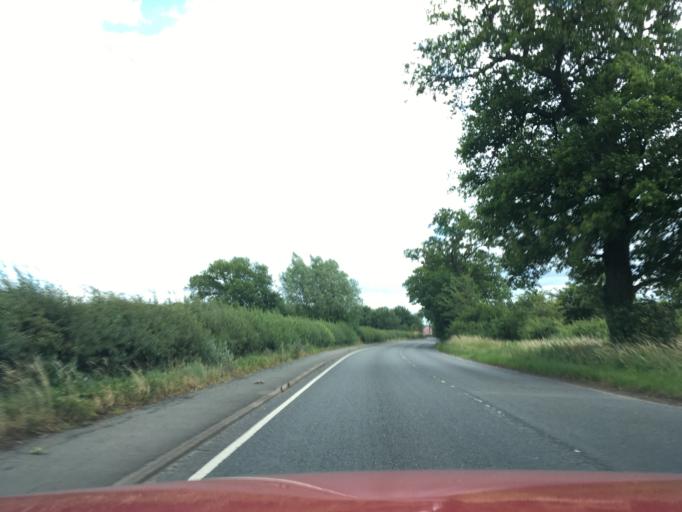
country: GB
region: England
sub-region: Warwickshire
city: Nuneaton
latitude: 52.5461
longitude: -1.4716
